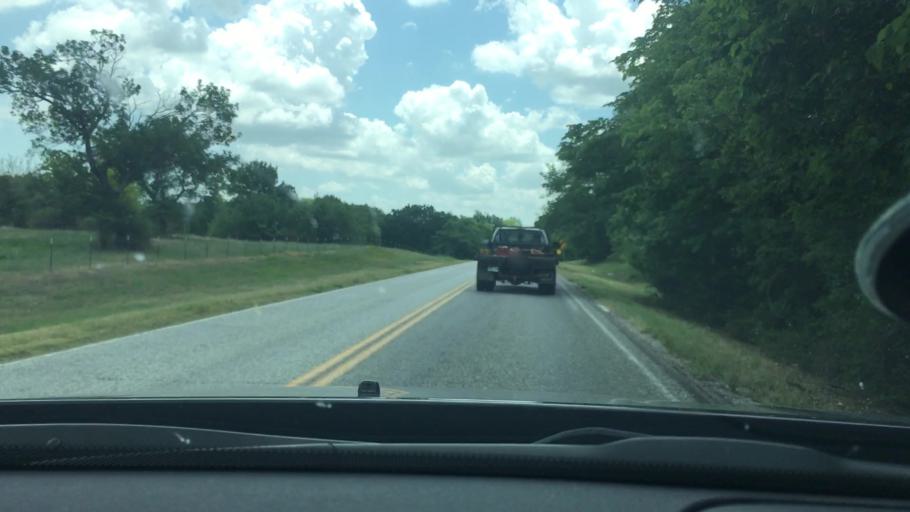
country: US
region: Oklahoma
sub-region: Pontotoc County
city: Ada
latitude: 34.5764
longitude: -96.6313
